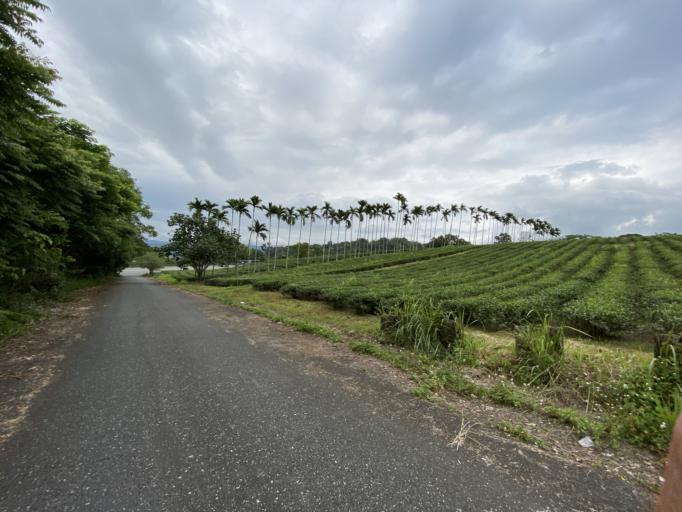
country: TW
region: Taiwan
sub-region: Hualien
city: Hualian
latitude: 23.4721
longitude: 121.3595
